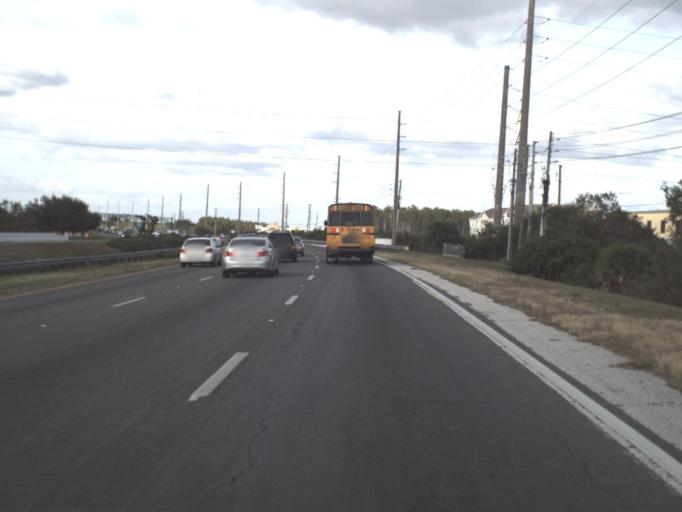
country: US
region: Florida
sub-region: Orange County
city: Williamsburg
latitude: 28.4122
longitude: -81.4233
